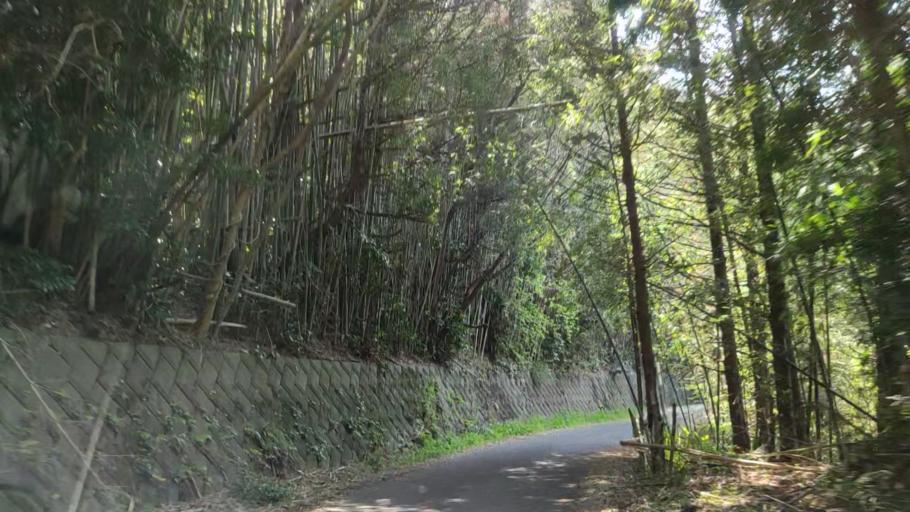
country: JP
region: Kanagawa
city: Ninomiya
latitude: 35.3267
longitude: 139.2671
